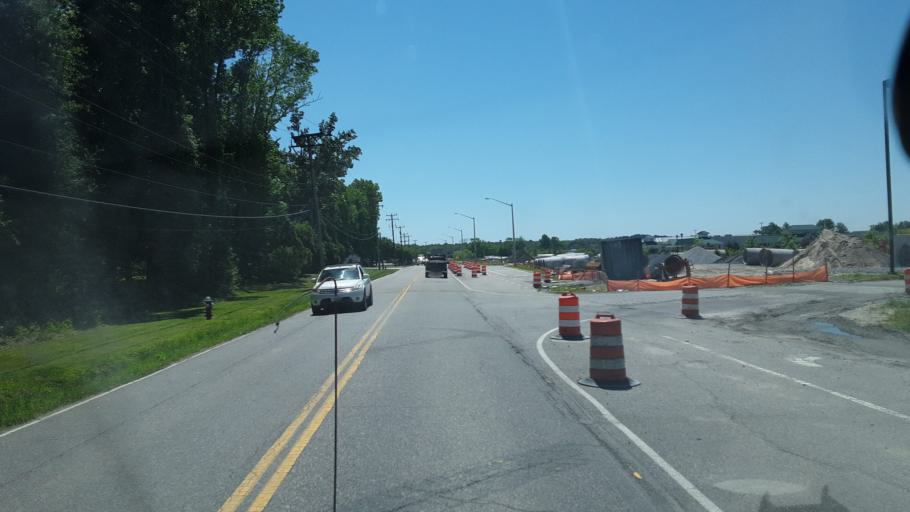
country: US
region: Virginia
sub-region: City of Virginia Beach
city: Virginia Beach
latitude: 36.7499
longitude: -76.0072
